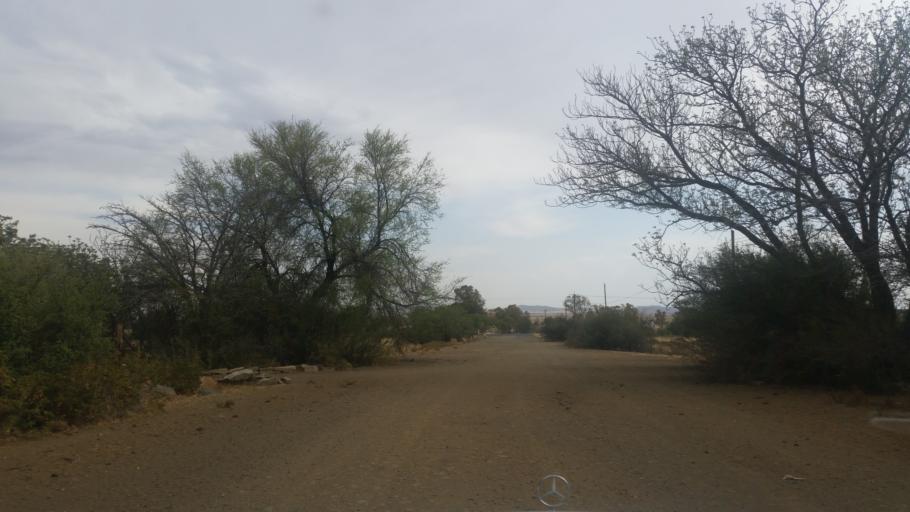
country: ZA
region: Orange Free State
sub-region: Xhariep District Municipality
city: Trompsburg
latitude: -30.4924
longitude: 25.9973
